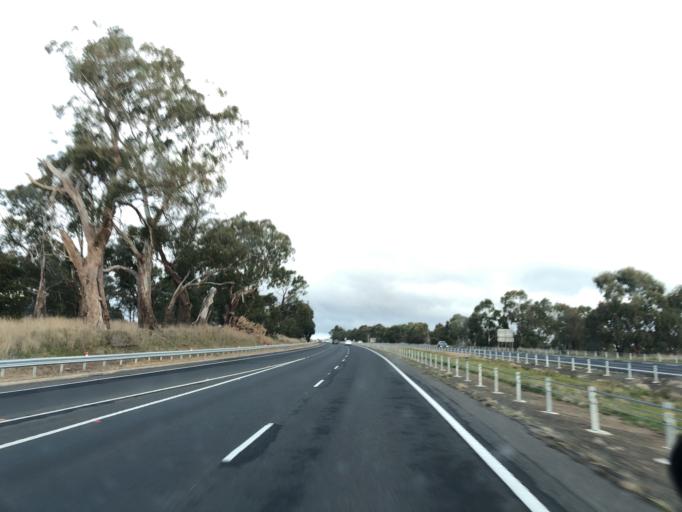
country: AU
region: Victoria
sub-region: Mount Alexander
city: Castlemaine
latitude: -37.2613
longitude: 144.4722
